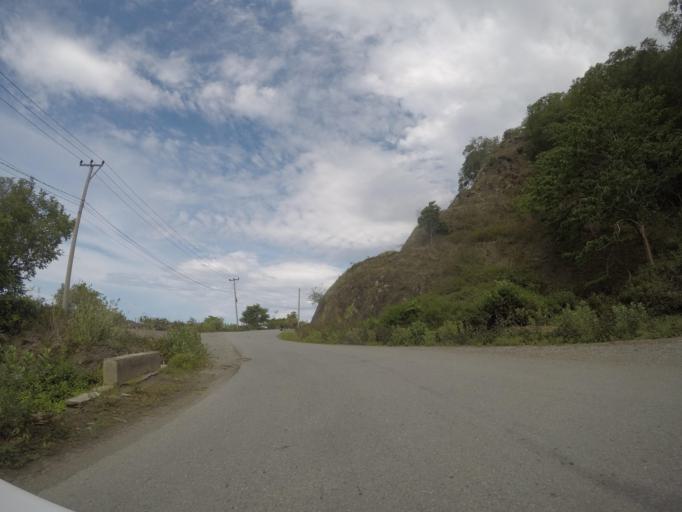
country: TL
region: Liquica
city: Maubara
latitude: -8.6312
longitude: 125.1512
